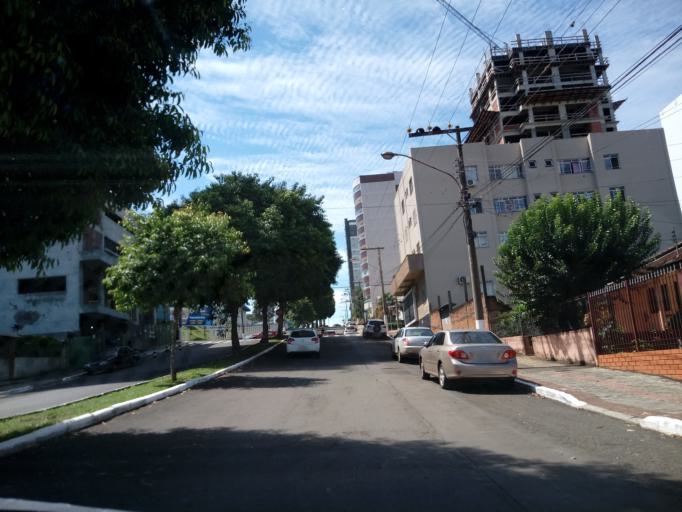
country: BR
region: Santa Catarina
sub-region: Chapeco
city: Chapeco
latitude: -27.1057
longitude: -52.6097
